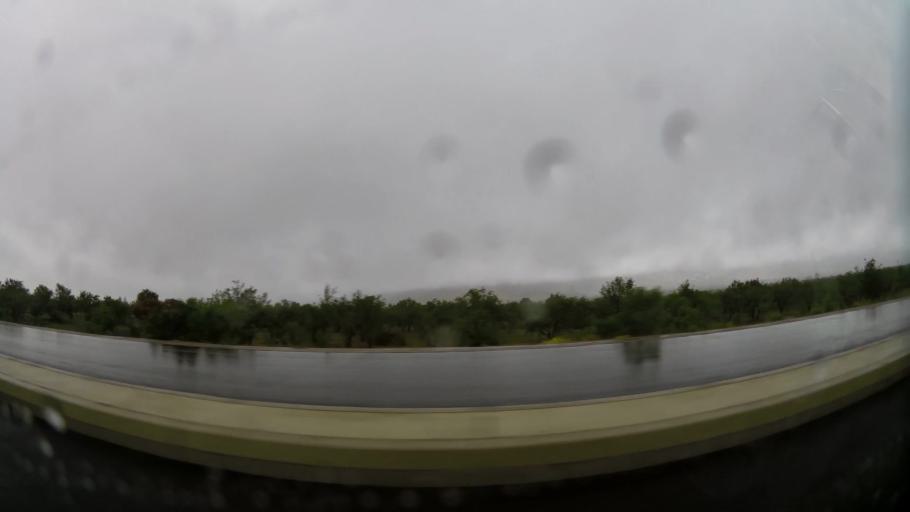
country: MA
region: Oriental
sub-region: Nador
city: Midar
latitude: 34.8544
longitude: -3.7220
